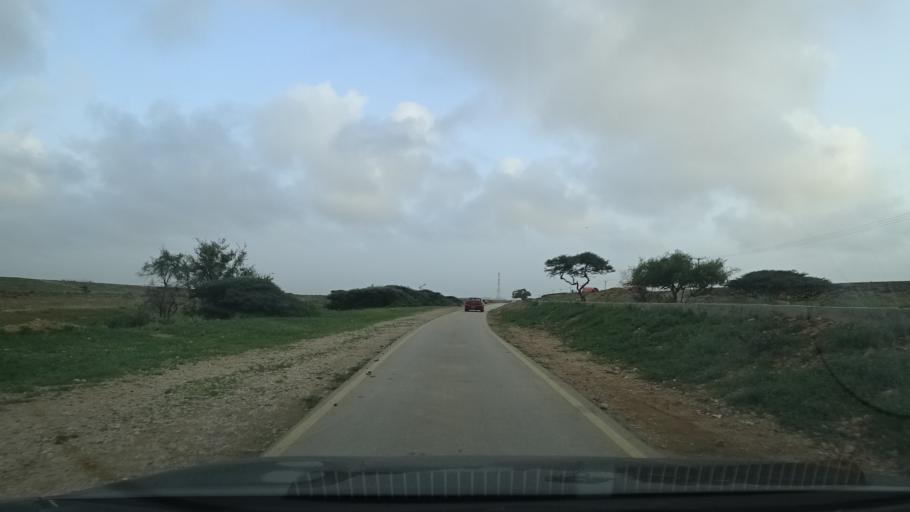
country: OM
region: Zufar
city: Salalah
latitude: 17.0937
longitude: 54.2333
